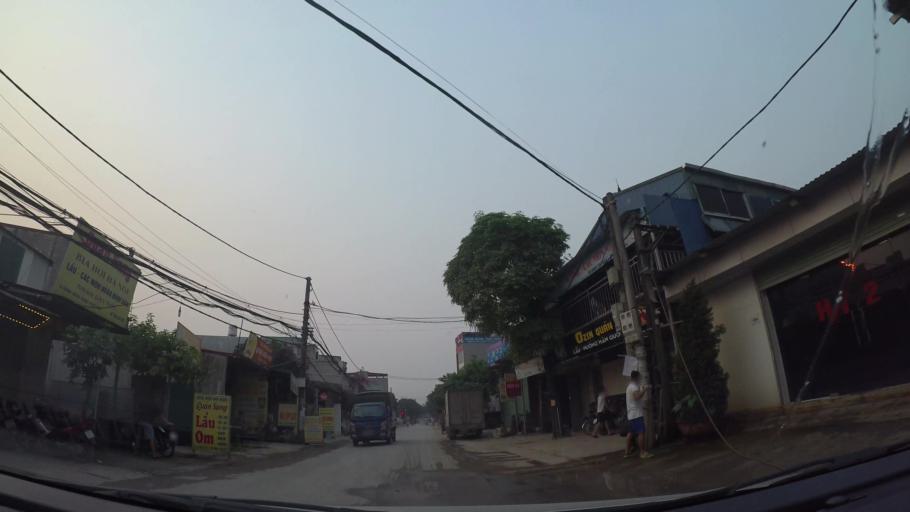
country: VN
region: Ha Noi
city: Ha Dong
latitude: 20.9910
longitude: 105.7248
